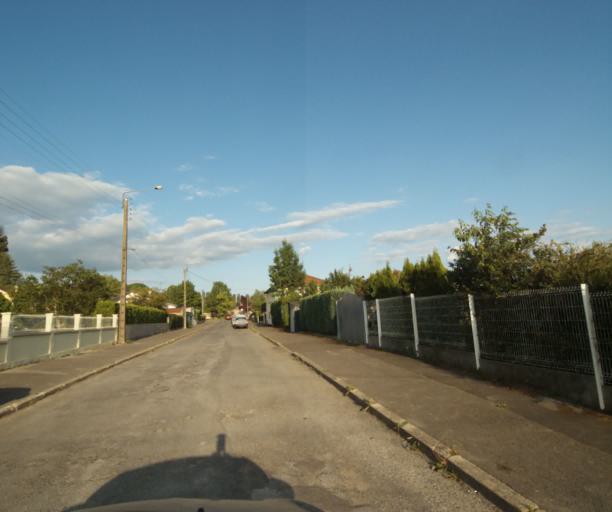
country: FR
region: Champagne-Ardenne
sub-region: Departement des Ardennes
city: Charleville-Mezieres
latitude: 49.7875
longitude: 4.7137
